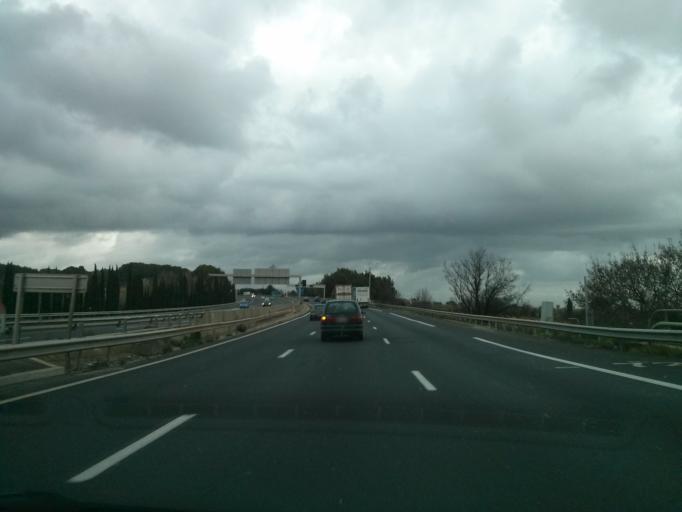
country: FR
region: Languedoc-Roussillon
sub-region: Departement du Gard
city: Aigues-Vives
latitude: 43.7294
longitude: 4.1887
